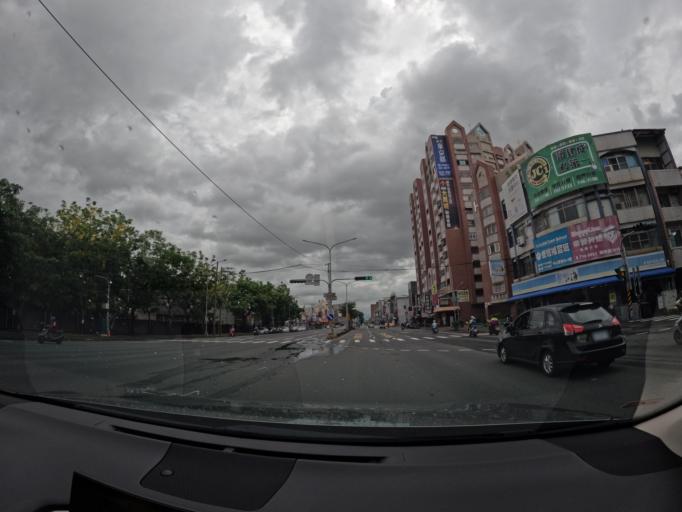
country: TW
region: Taiwan
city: Fengshan
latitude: 22.6248
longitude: 120.3724
